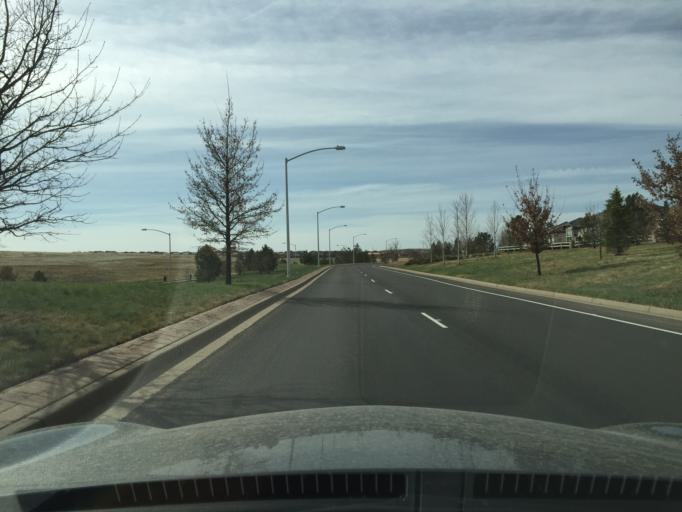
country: US
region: Colorado
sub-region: Boulder County
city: Lafayette
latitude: 39.9947
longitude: -105.0386
